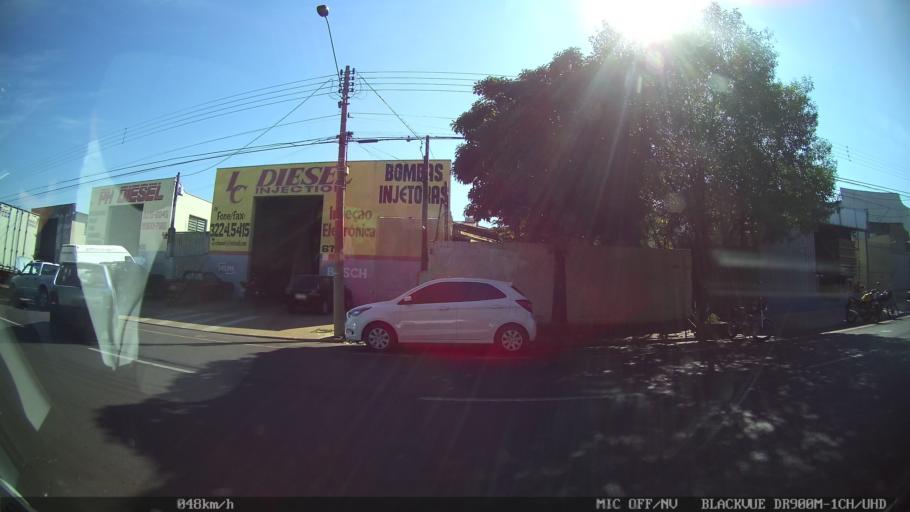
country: BR
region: Sao Paulo
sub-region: Sao Jose Do Rio Preto
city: Sao Jose do Rio Preto
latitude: -20.7859
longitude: -49.3714
